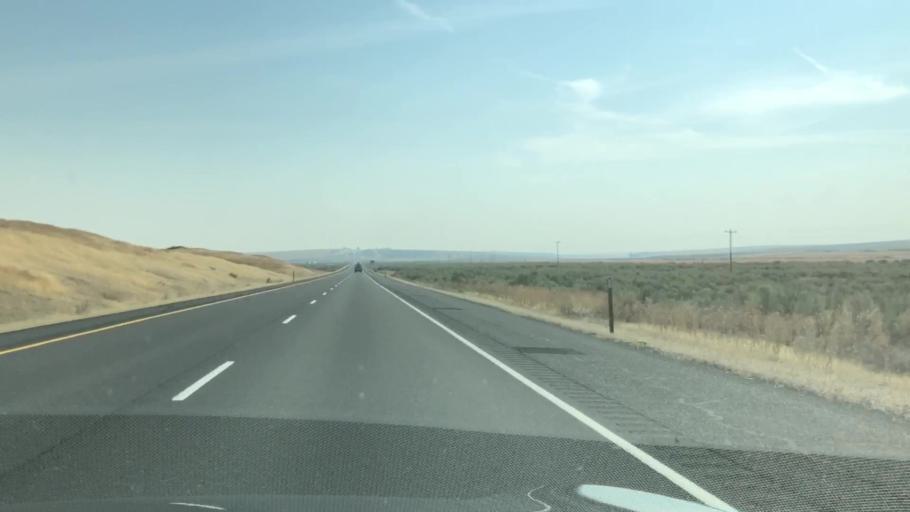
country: US
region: Washington
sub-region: Grant County
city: Warden
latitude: 47.0871
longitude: -118.9117
